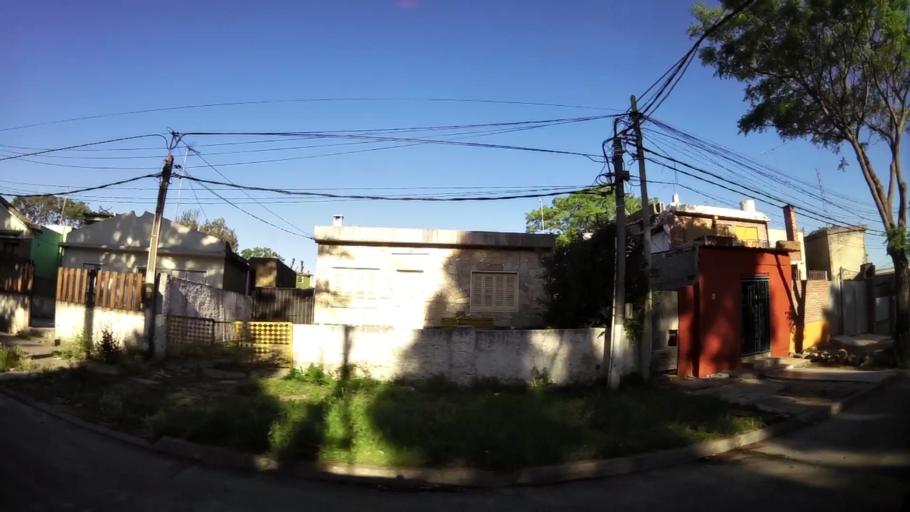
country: UY
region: Montevideo
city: Montevideo
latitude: -34.8424
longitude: -56.2165
